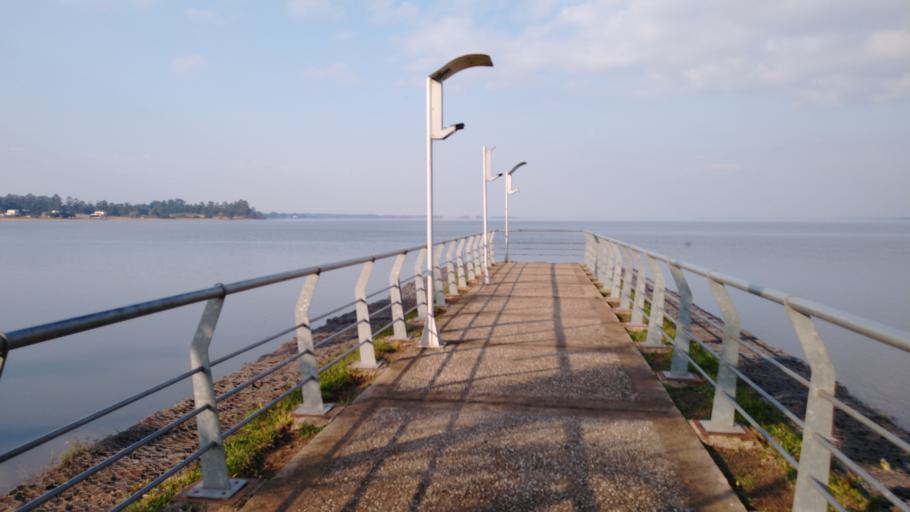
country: AR
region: Entre Rios
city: Santa Ana
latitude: -30.9127
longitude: -57.9245
